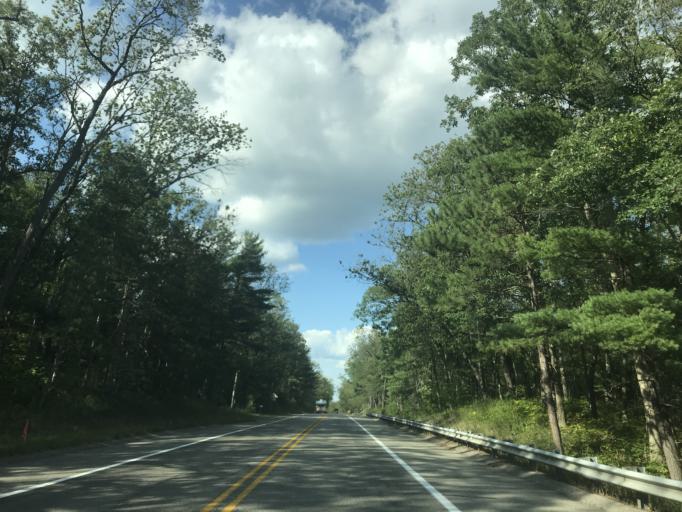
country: US
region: Michigan
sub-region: Newaygo County
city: Newaygo
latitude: 43.4601
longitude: -85.7779
